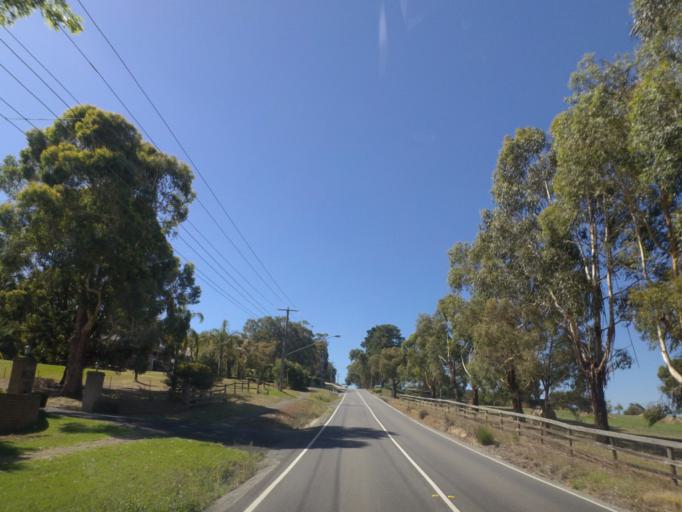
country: AU
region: Victoria
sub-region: Yarra Ranges
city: Chirnside Park
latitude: -37.7376
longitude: 145.2824
